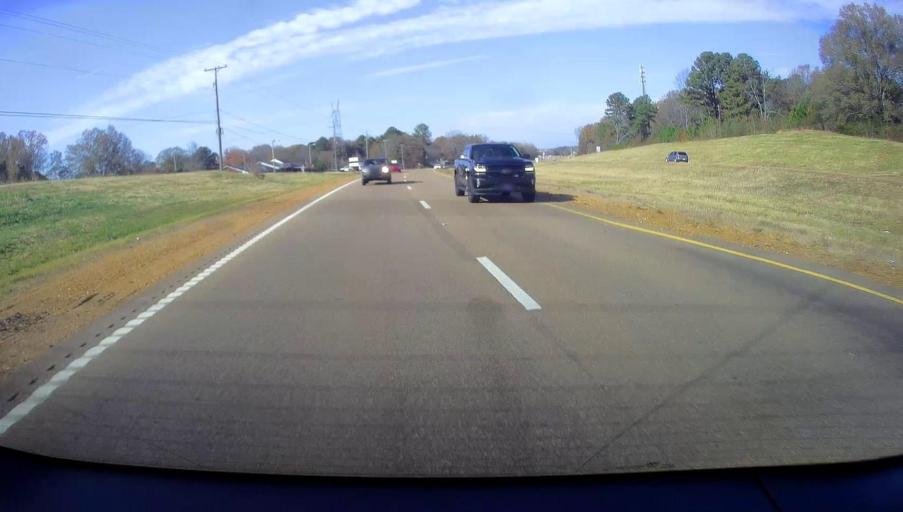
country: US
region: Tennessee
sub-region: Fayette County
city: Piperton
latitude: 34.9889
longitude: -89.6095
